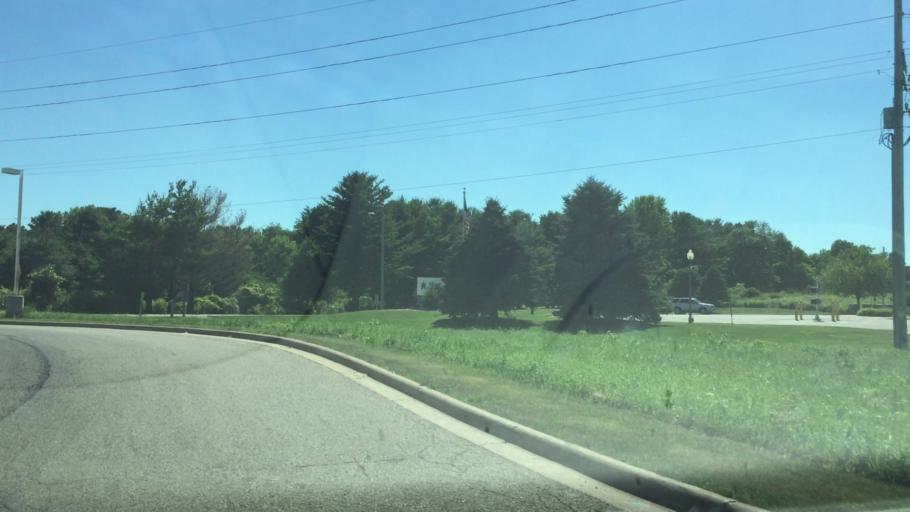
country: US
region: Wisconsin
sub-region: Dane County
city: Verona
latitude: 42.9709
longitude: -89.5137
